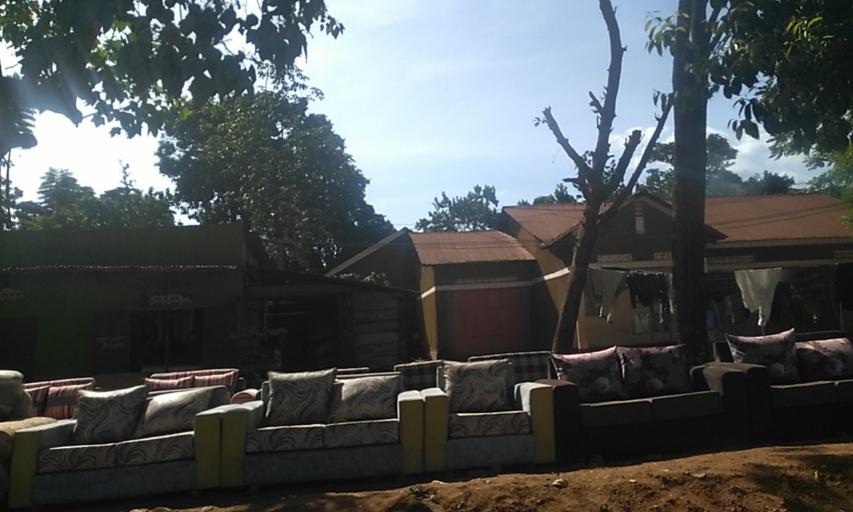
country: UG
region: Central Region
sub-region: Wakiso District
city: Kireka
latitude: 0.3769
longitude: 32.6254
